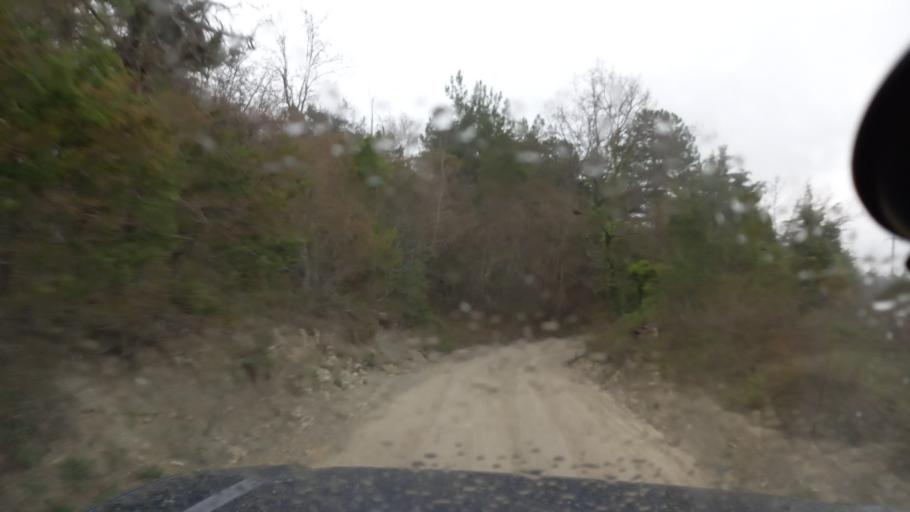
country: RU
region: Krasnodarskiy
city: Dzhubga
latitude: 44.3205
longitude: 38.6798
